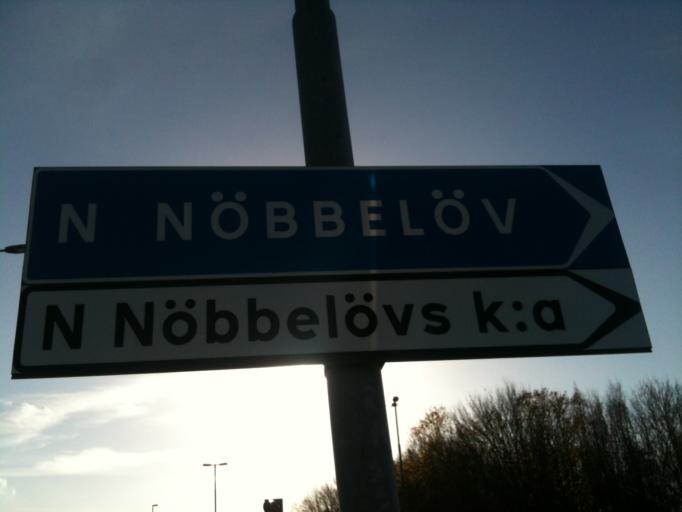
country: SE
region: Skane
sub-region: Lunds Kommun
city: Lund
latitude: 55.7340
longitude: 13.1757
